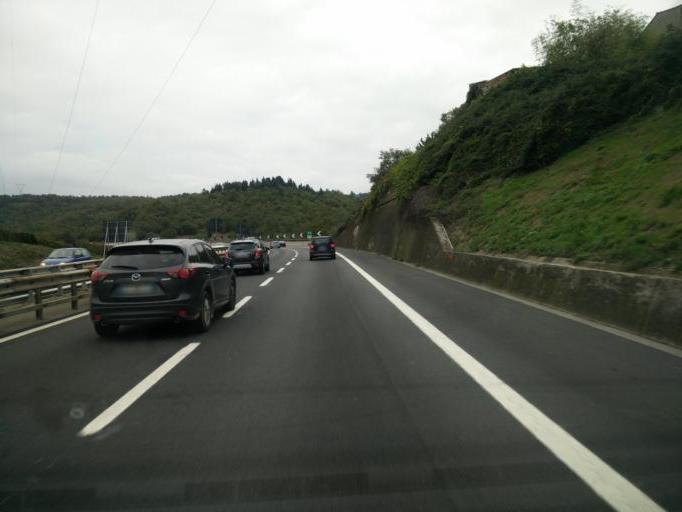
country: IT
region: Tuscany
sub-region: Province of Florence
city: Cavallina
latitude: 43.9338
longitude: 11.2205
